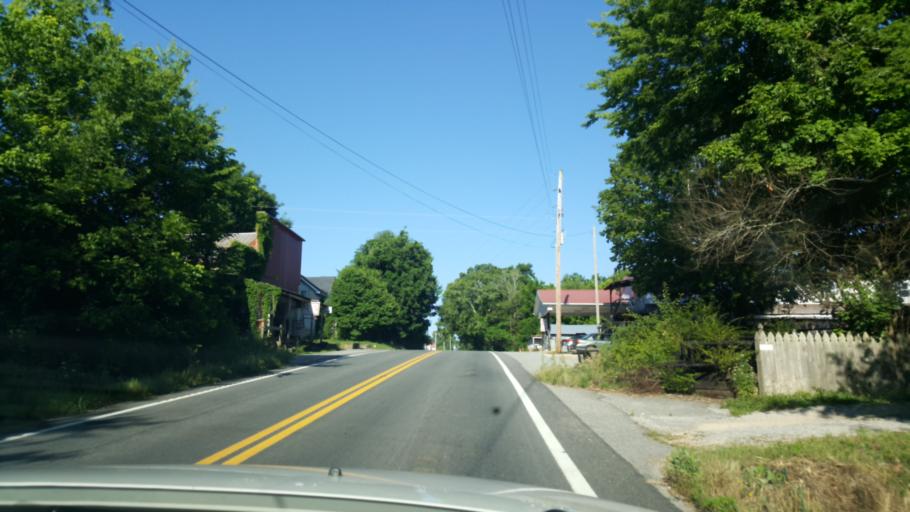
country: US
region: Tennessee
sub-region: Lawrence County
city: Lawrenceburg
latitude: 35.3924
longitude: -87.3940
